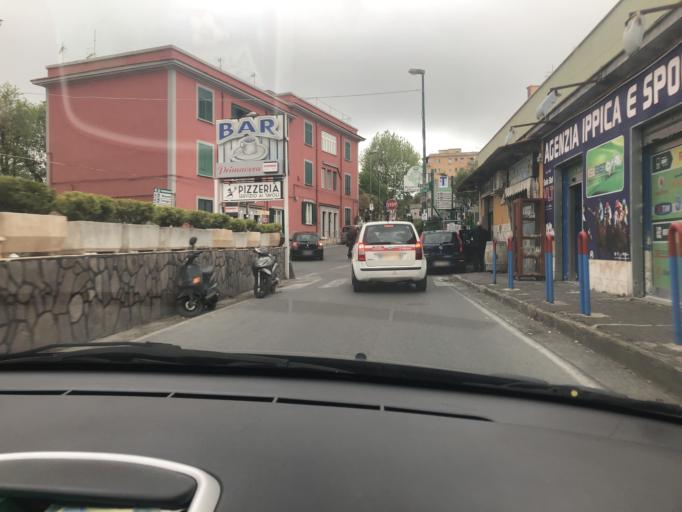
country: IT
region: Campania
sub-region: Provincia di Napoli
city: Torre Caracciolo
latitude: 40.8658
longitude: 14.1894
